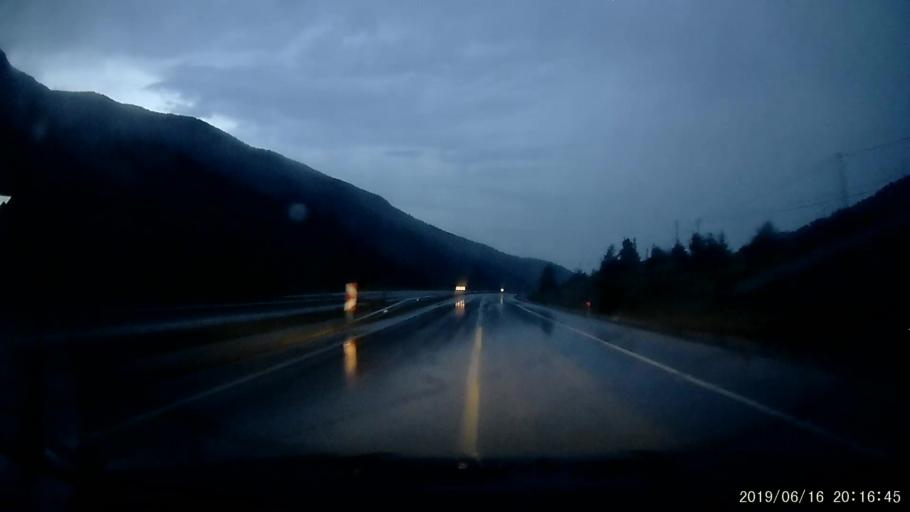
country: TR
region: Tokat
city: Resadiye
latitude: 40.3607
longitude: 37.4350
